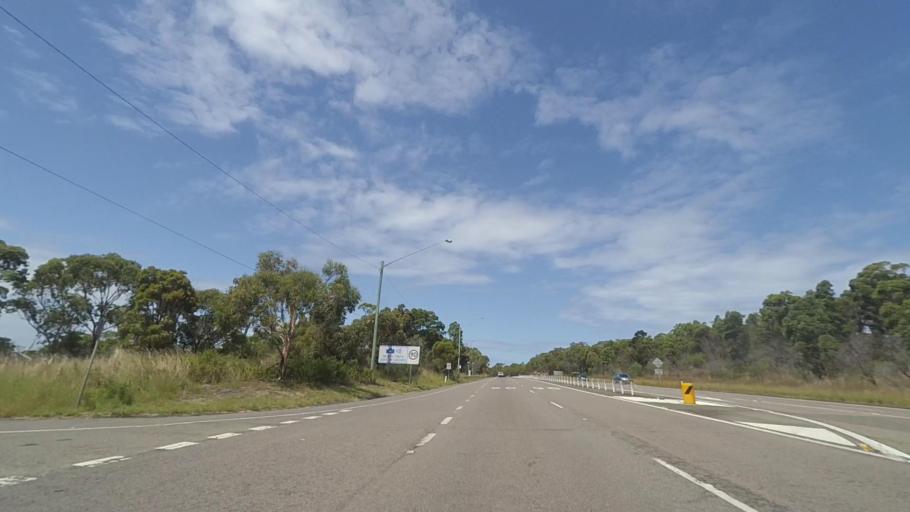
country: AU
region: New South Wales
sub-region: Wyong Shire
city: Kingfisher Shores
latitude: -33.1344
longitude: 151.6122
